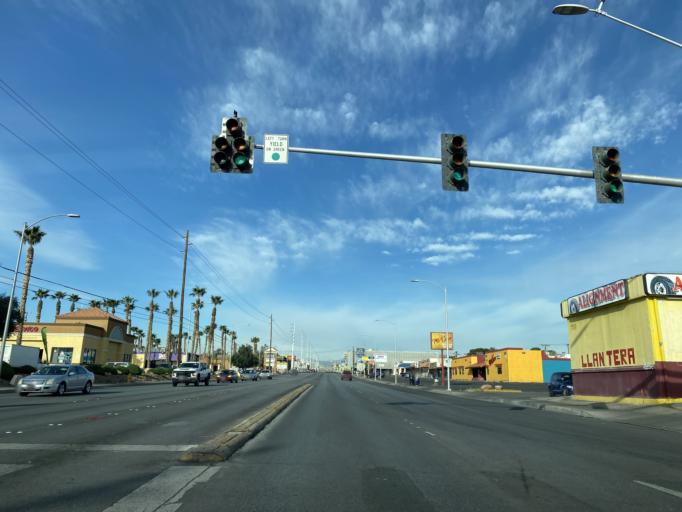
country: US
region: Nevada
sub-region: Clark County
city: Las Vegas
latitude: 36.1589
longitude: -115.1250
